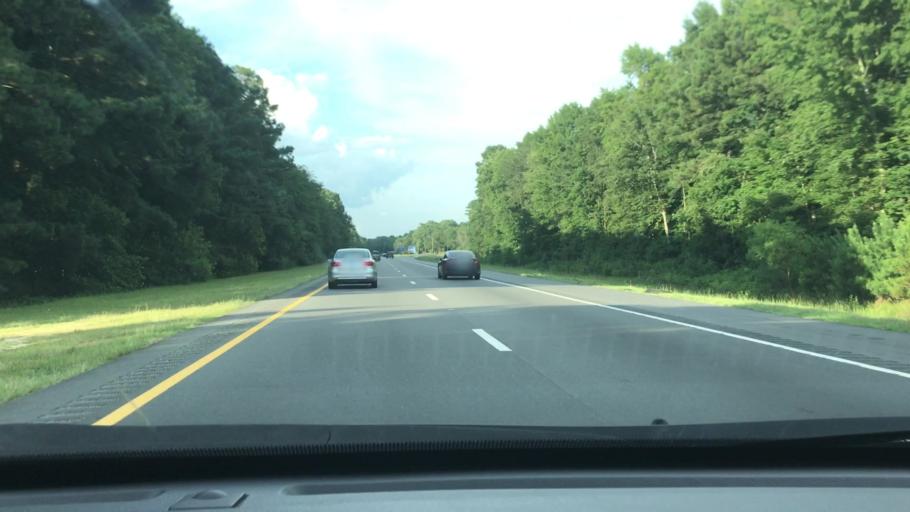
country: US
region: North Carolina
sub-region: Cumberland County
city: Vander
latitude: 34.9925
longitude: -78.8344
